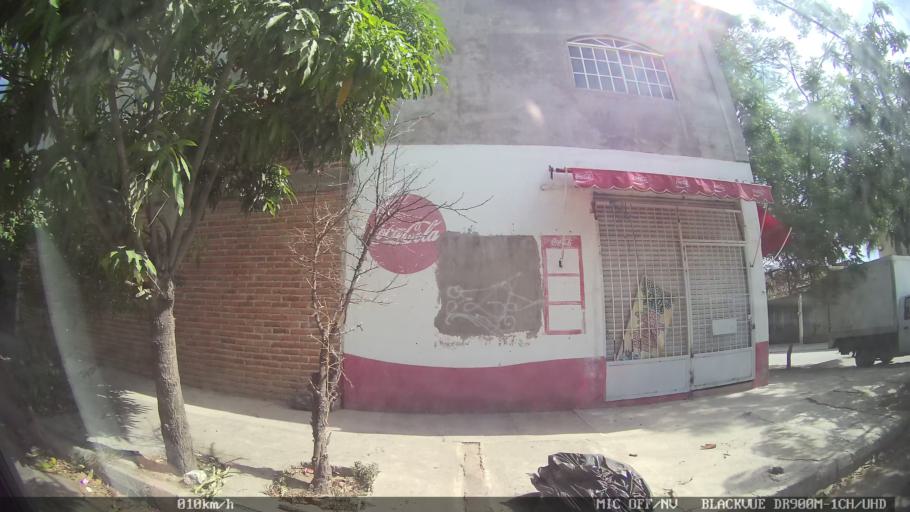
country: MX
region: Jalisco
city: Tonala
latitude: 20.6720
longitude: -103.2515
